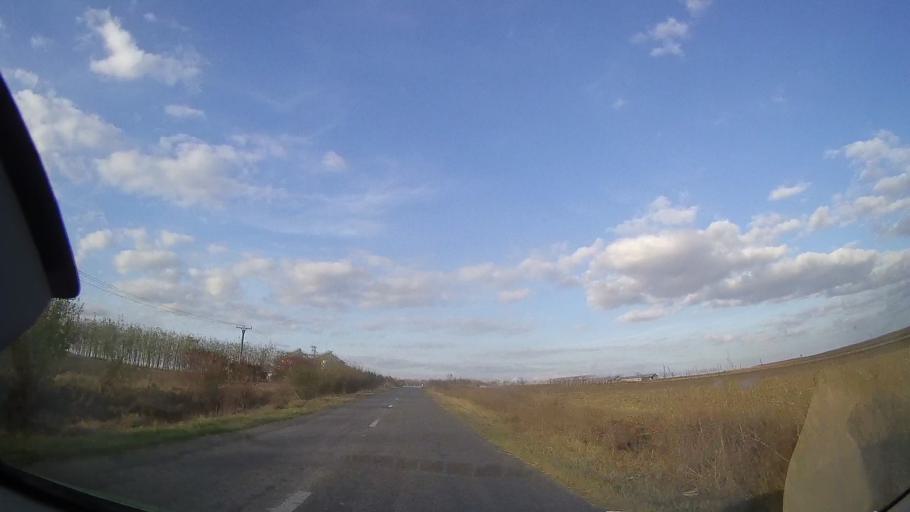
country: RO
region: Constanta
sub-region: Comuna Dumbraveni
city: Dumbraveni
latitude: 43.9242
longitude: 28.0296
